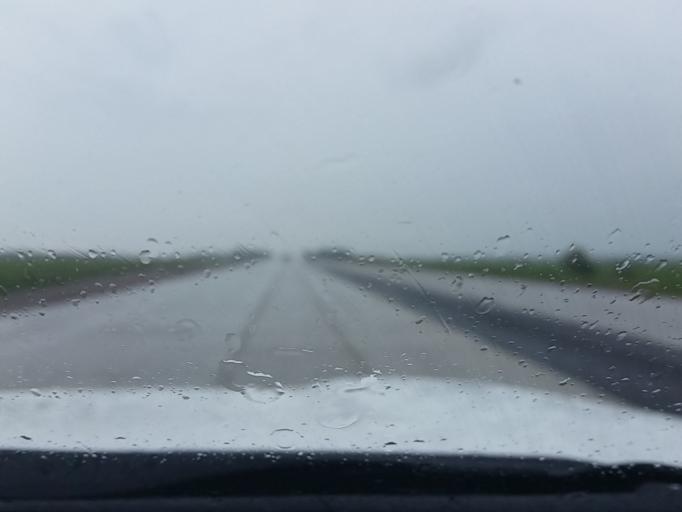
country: KZ
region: Almaty Oblysy
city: Turgen'
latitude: 43.5519
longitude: 77.7746
